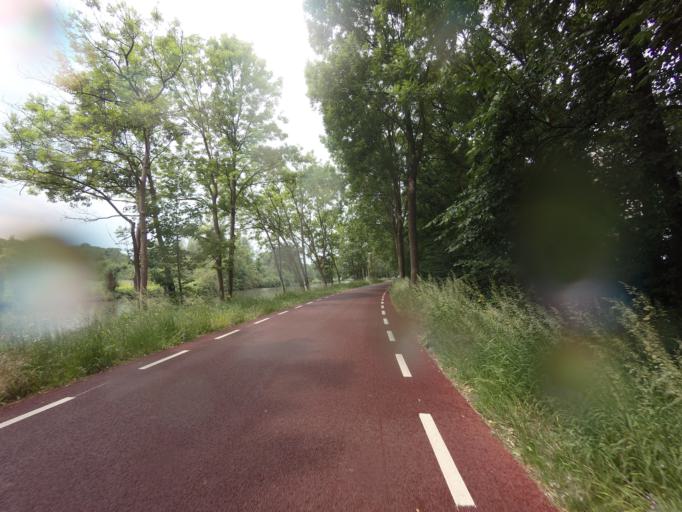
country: NL
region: Utrecht
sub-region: Stichtse Vecht
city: Maarssen
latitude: 52.1228
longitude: 5.0742
